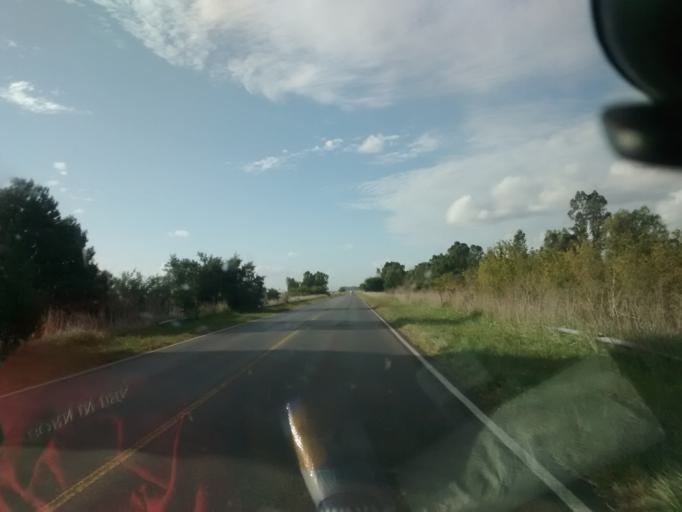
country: AR
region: Buenos Aires
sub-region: Partido de Ayacucho
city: Ayacucho
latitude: -36.7079
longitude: -58.5743
